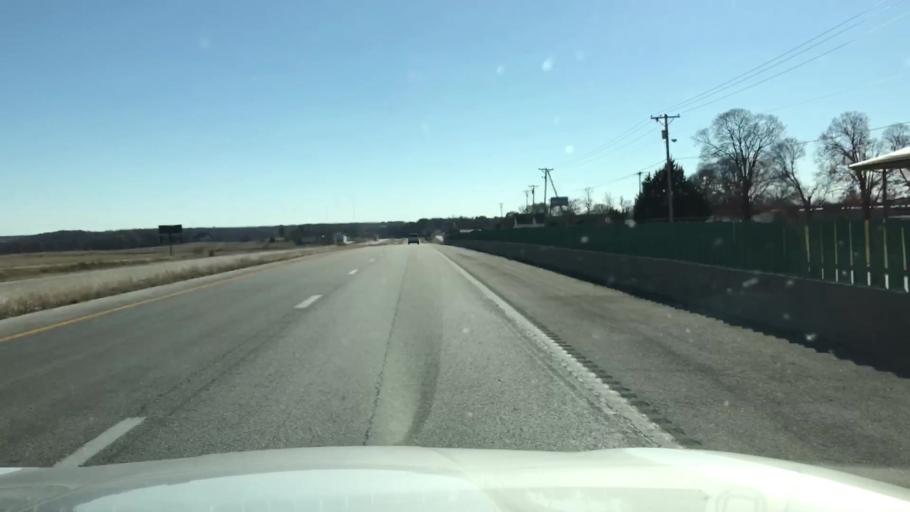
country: US
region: Missouri
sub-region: Jasper County
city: Carthage
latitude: 37.1239
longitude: -94.3111
